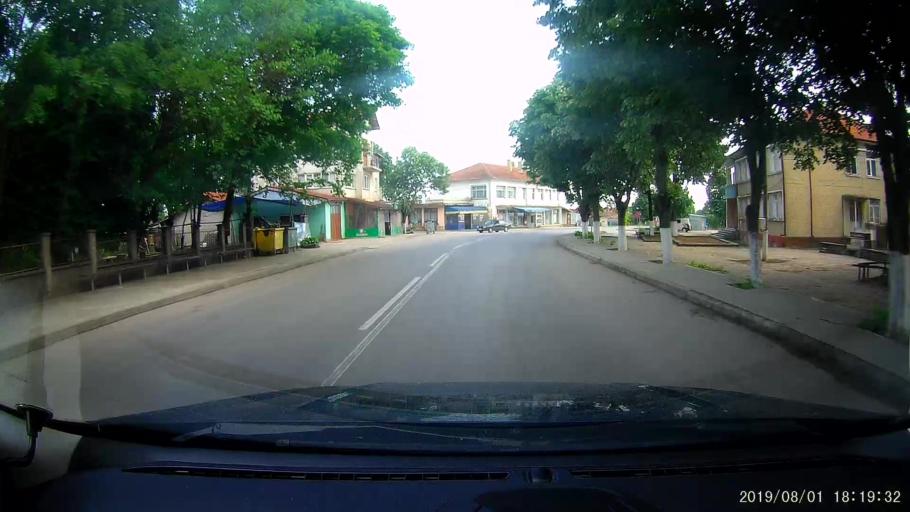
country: BG
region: Shumen
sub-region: Obshtina Kaolinovo
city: Kaolinovo
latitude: 43.6825
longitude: 27.0911
